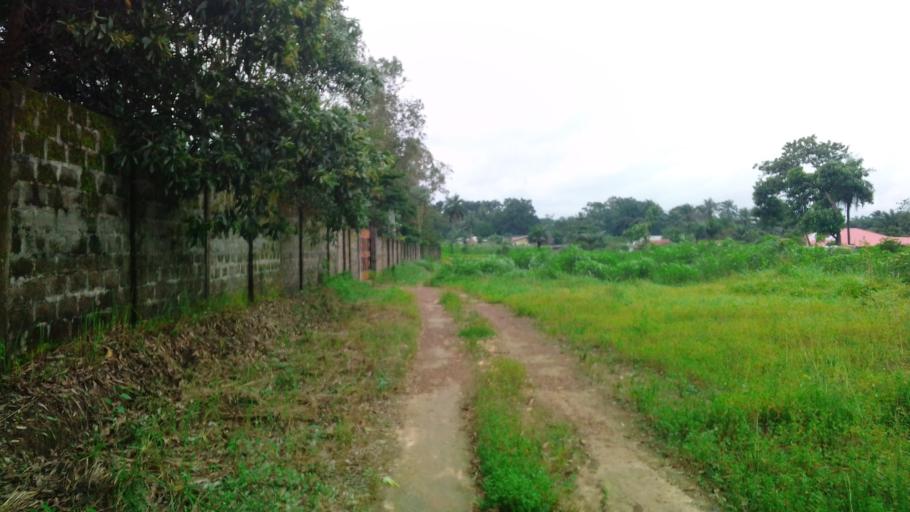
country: SL
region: Northern Province
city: Lunsar
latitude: 8.6966
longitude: -12.5485
